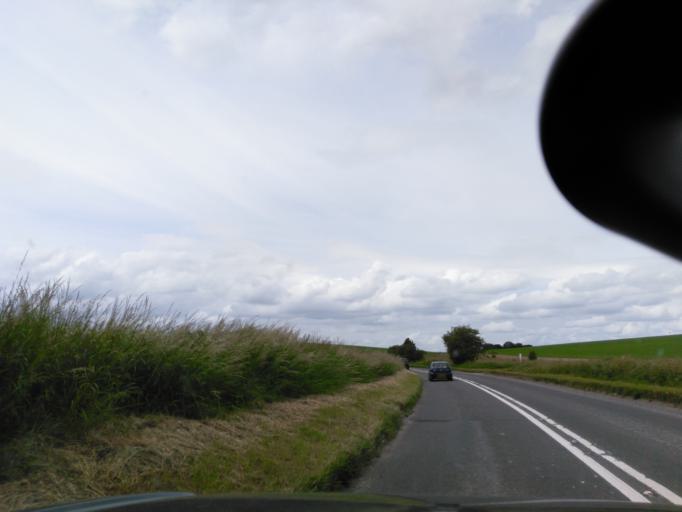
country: GB
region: England
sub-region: Wiltshire
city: Market Lavington
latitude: 51.2406
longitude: -1.9749
